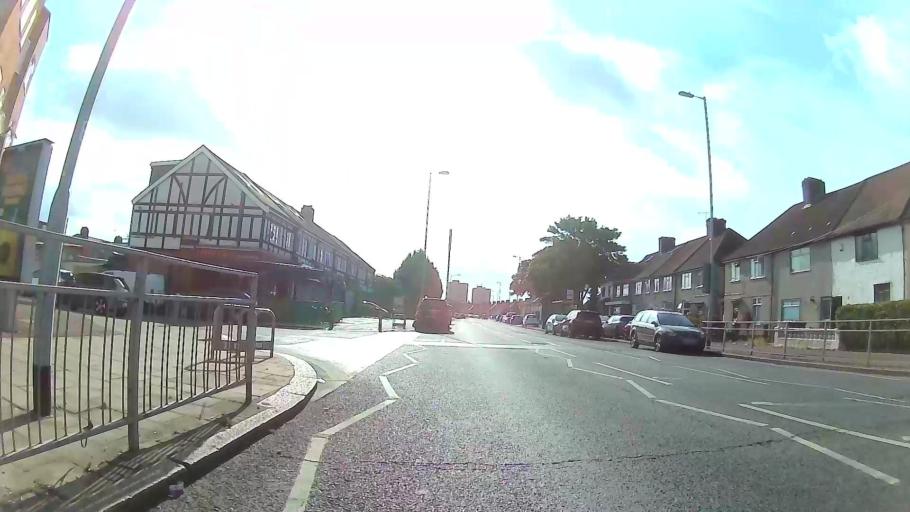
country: GB
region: England
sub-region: Greater London
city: Chadwell Heath
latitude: 51.5613
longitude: 0.1404
